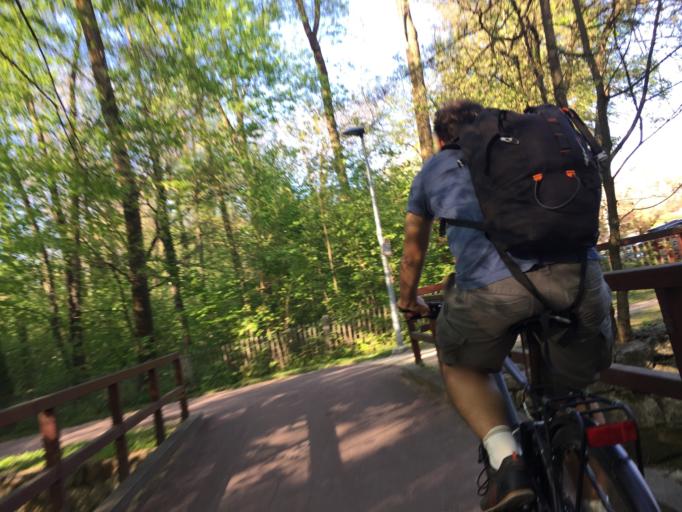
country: FR
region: Rhone-Alpes
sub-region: Departement de la Savoie
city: Chambery
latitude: 45.5643
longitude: 5.9391
